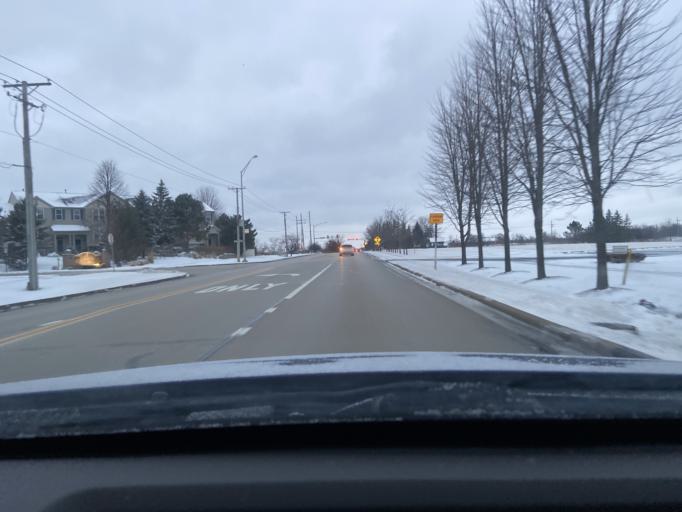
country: US
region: Illinois
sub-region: Lake County
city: Third Lake
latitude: 42.3586
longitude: -88.0241
